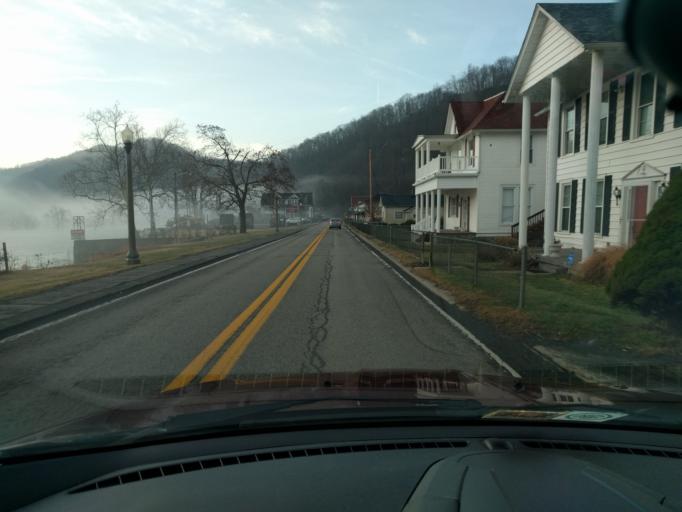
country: US
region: West Virginia
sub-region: Fayette County
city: Ansted
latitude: 38.1523
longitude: -81.2151
